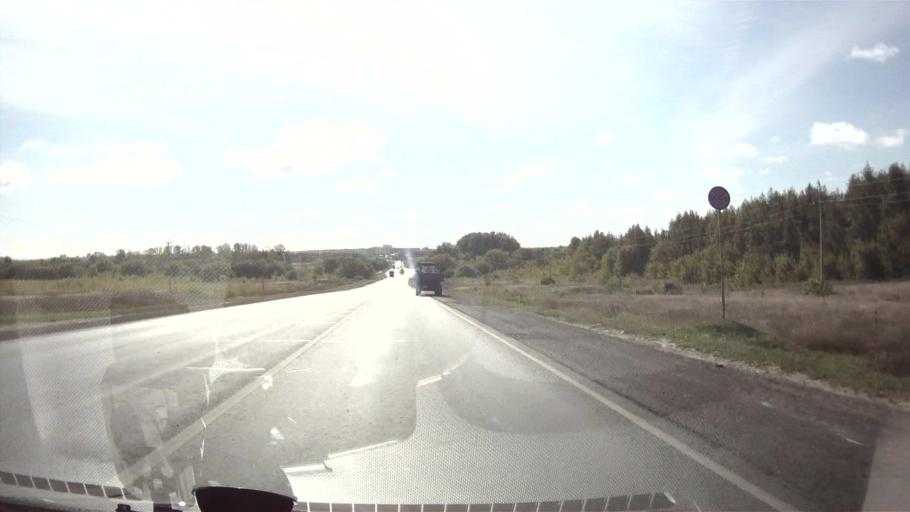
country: RU
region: Ulyanovsk
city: Isheyevka
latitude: 54.3080
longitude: 48.2387
